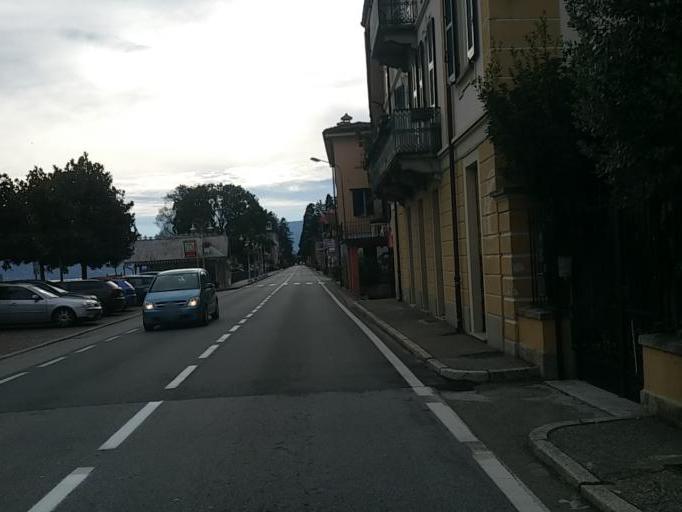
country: IT
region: Piedmont
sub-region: Provincia Verbano-Cusio-Ossola
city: Ghiffa
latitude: 45.9578
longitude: 8.6193
